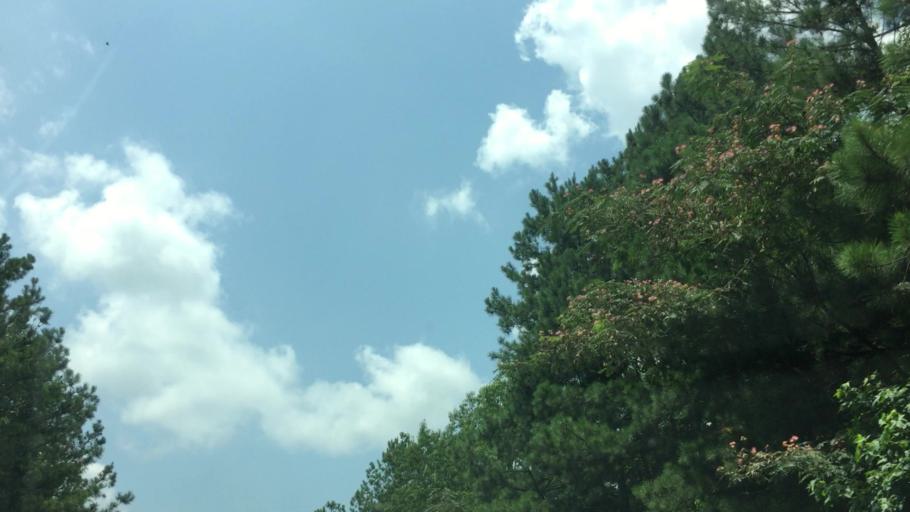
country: US
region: Georgia
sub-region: Carroll County
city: Villa Rica
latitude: 33.6178
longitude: -84.9528
